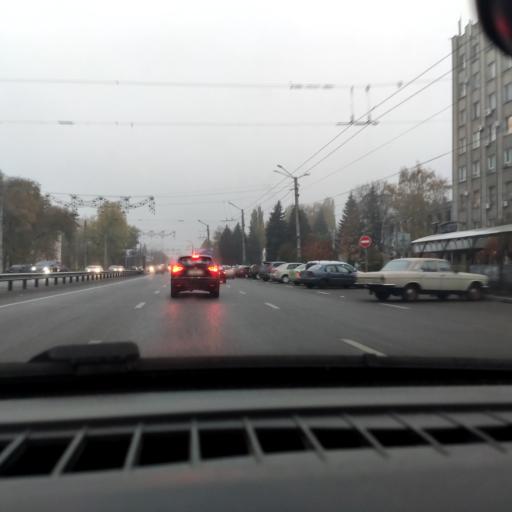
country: RU
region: Voronezj
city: Voronezh
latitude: 51.6542
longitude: 39.1717
